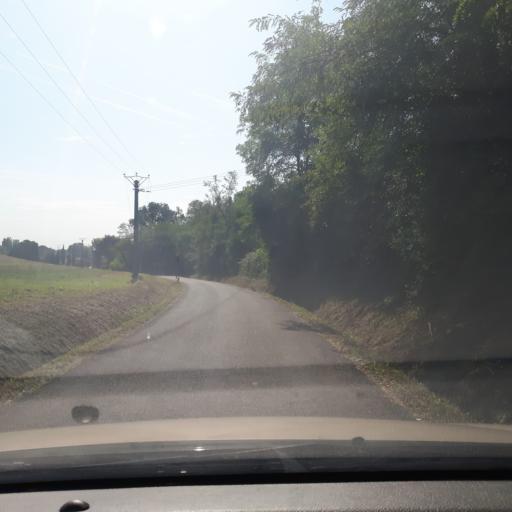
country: FR
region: Midi-Pyrenees
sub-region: Departement de la Haute-Garonne
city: Villeneuve-les-Bouloc
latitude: 43.7697
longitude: 1.4114
